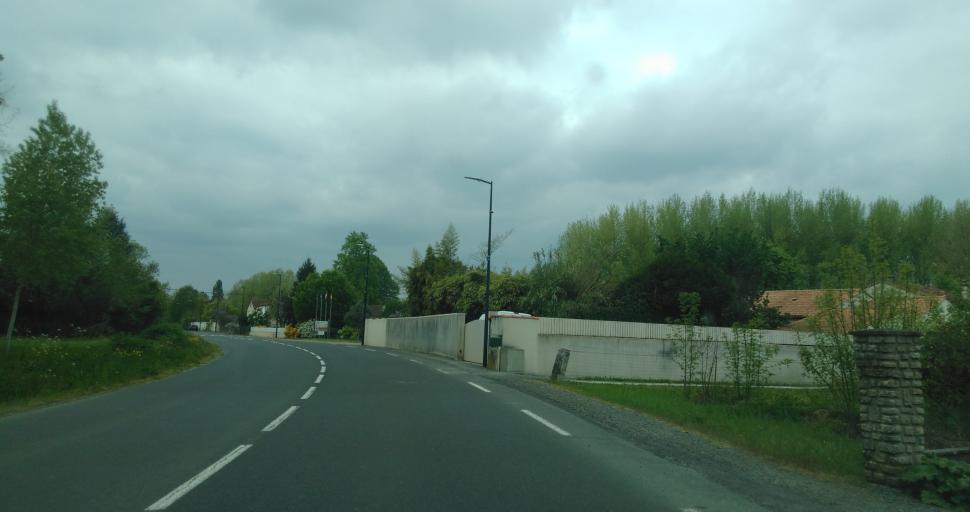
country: FR
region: Poitou-Charentes
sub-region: Departement des Deux-Sevres
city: Magne
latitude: 46.3128
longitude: -0.5316
